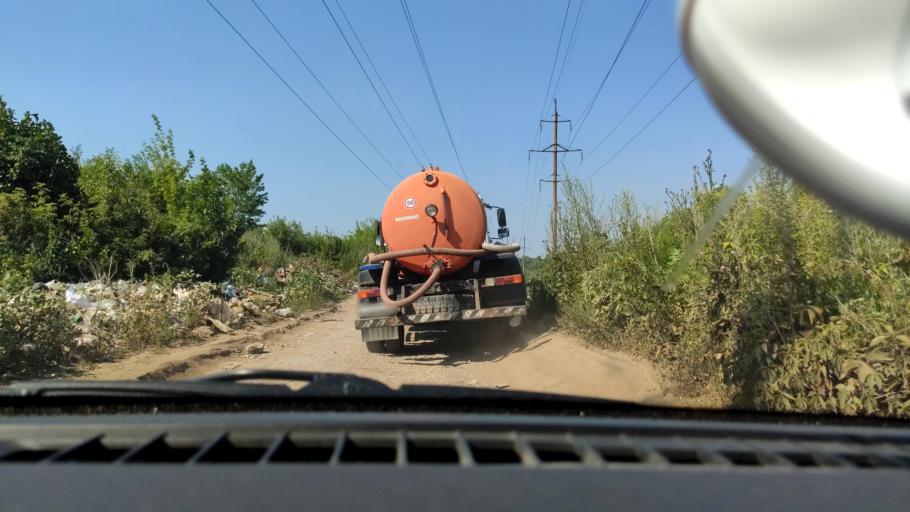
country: RU
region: Samara
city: Petra-Dubrava
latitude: 53.2662
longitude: 50.3003
